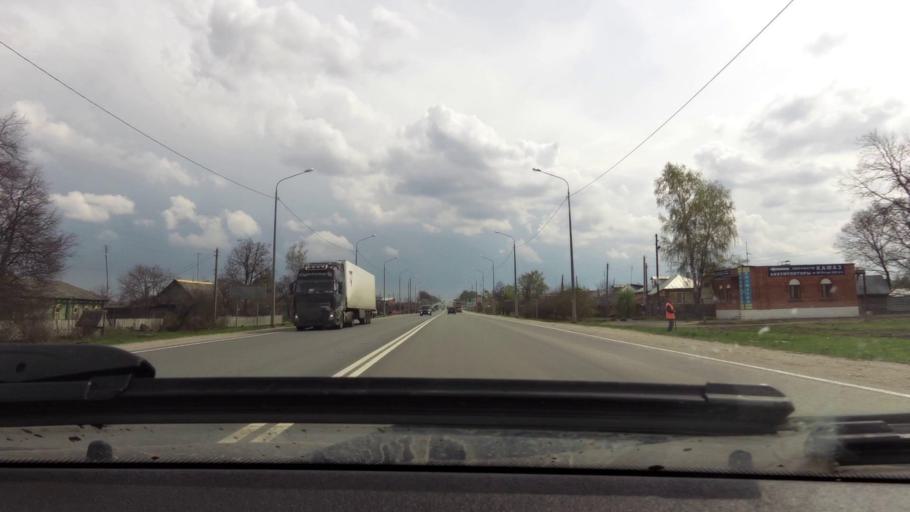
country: RU
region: Rjazan
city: Bagramovo
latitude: 54.7315
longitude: 39.4614
